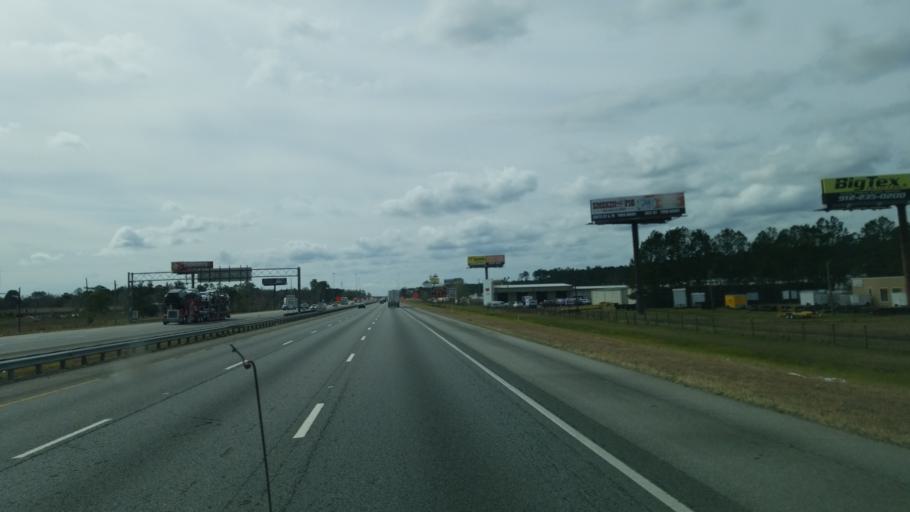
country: US
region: Georgia
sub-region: Bryan County
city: Richmond Hill
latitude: 31.9668
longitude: -81.3225
